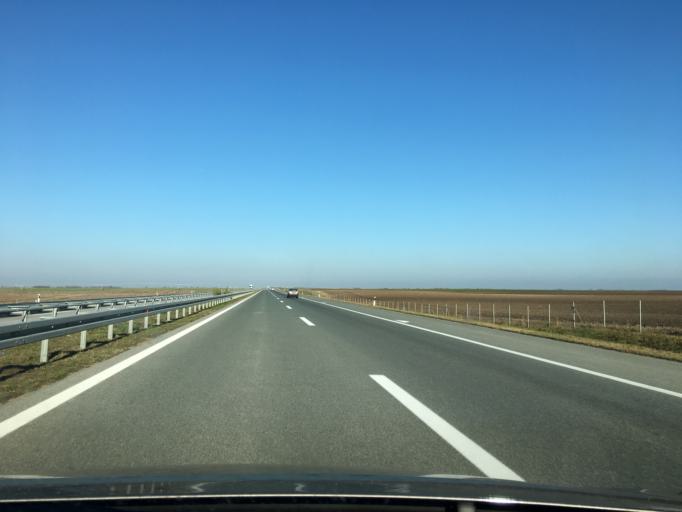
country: RS
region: Autonomna Pokrajina Vojvodina
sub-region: Severnobacki Okrug
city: Mali Igos
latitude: 45.7061
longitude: 19.7174
